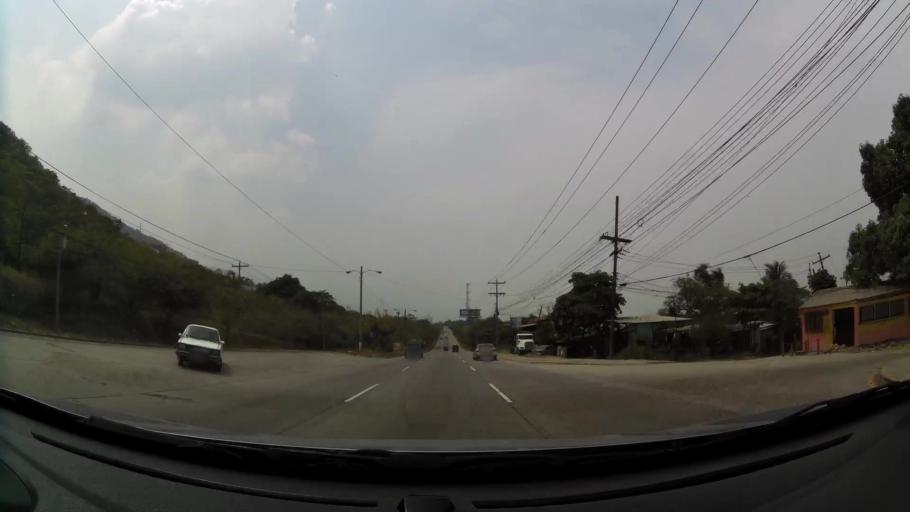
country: HN
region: Cortes
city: Chotepe
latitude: 15.4464
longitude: -88.0216
